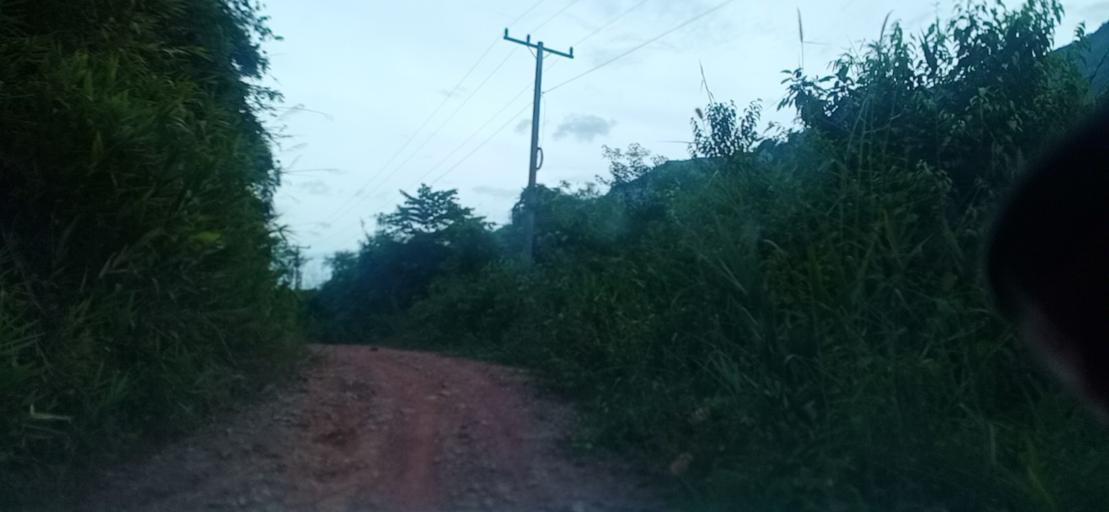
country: TH
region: Changwat Bueng Kan
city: Pak Khat
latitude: 18.5606
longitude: 103.2528
